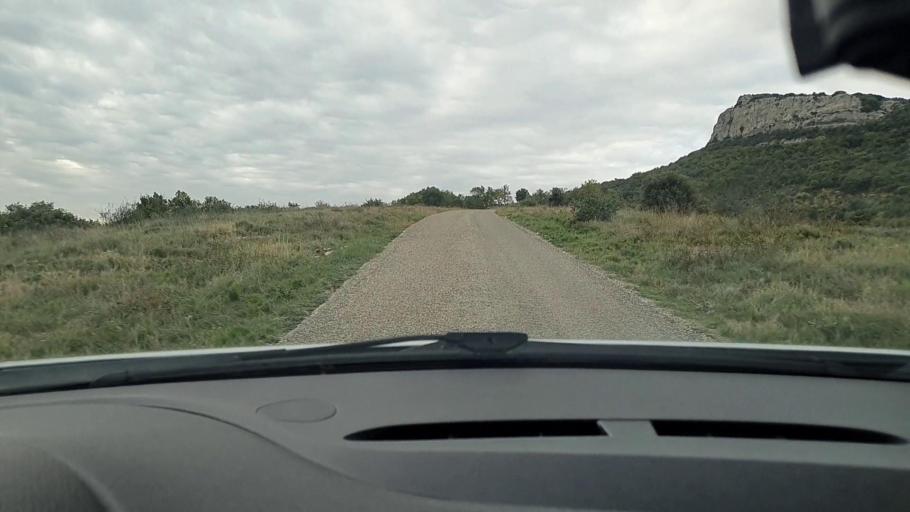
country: FR
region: Languedoc-Roussillon
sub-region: Departement du Gard
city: Mons
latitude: 44.1490
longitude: 4.2911
